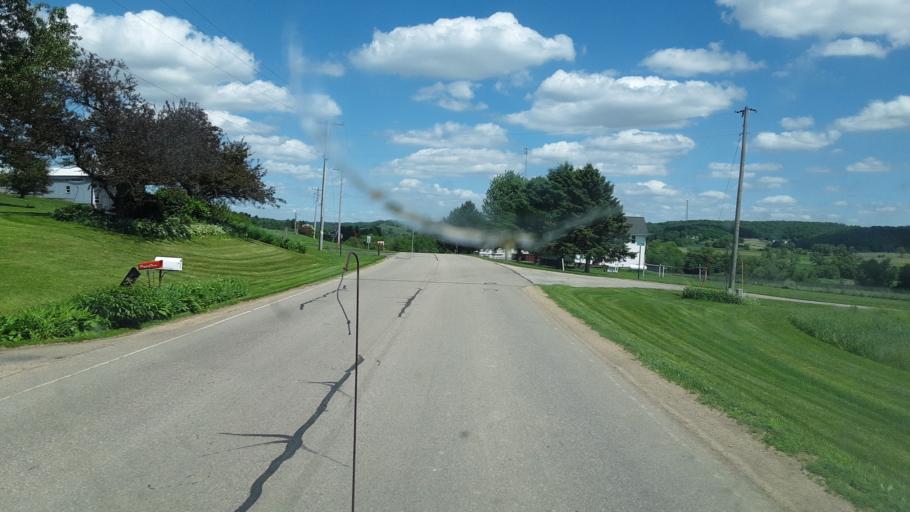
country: US
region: Wisconsin
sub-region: Vernon County
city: Hillsboro
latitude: 43.5258
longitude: -90.2172
